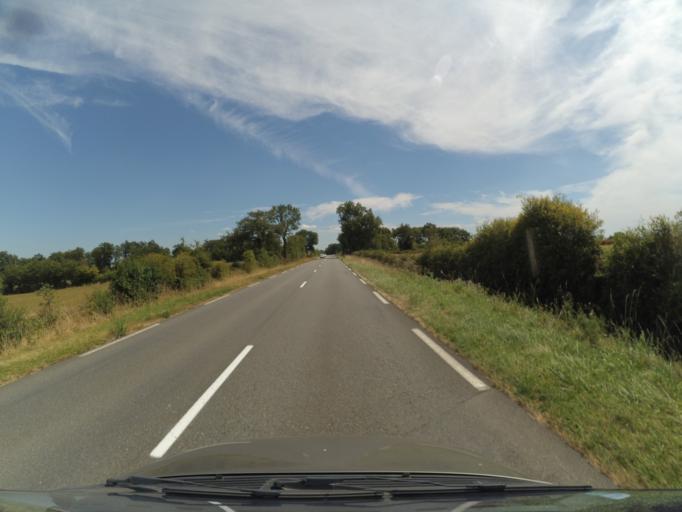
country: FR
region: Poitou-Charentes
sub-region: Departement de la Charente
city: Confolens
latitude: 46.0431
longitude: 0.6260
